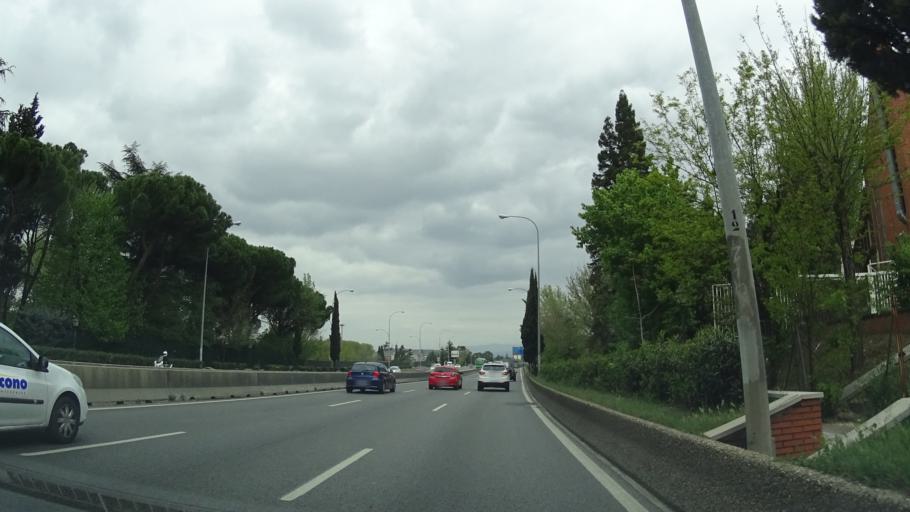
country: ES
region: Madrid
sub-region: Provincia de Madrid
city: Moncloa-Aravaca
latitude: 40.4424
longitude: -3.7305
